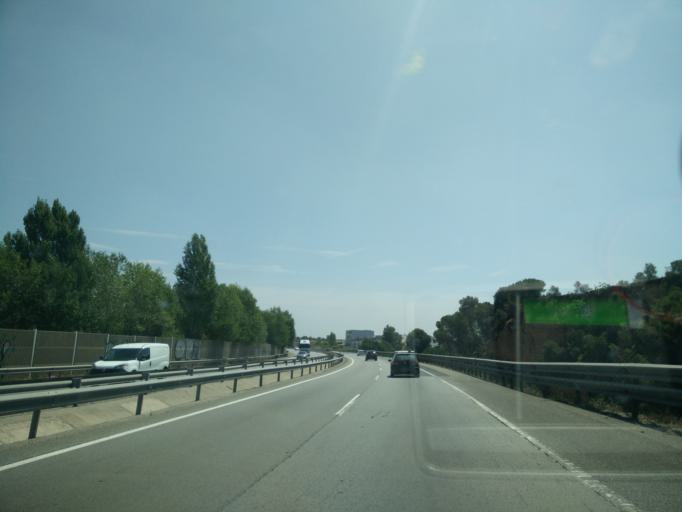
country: ES
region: Catalonia
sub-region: Provincia de Barcelona
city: Esparreguera
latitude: 41.5317
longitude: 1.8675
